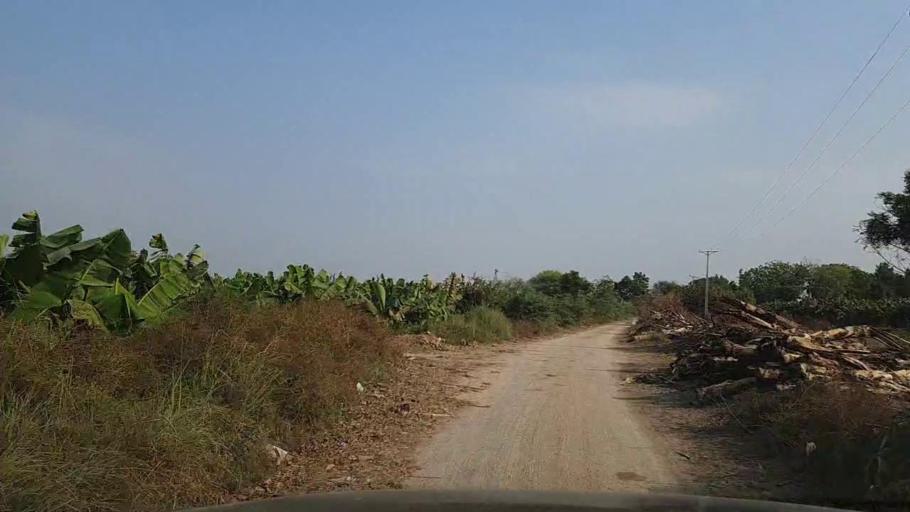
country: PK
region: Sindh
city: Thatta
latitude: 24.6457
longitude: 67.9376
